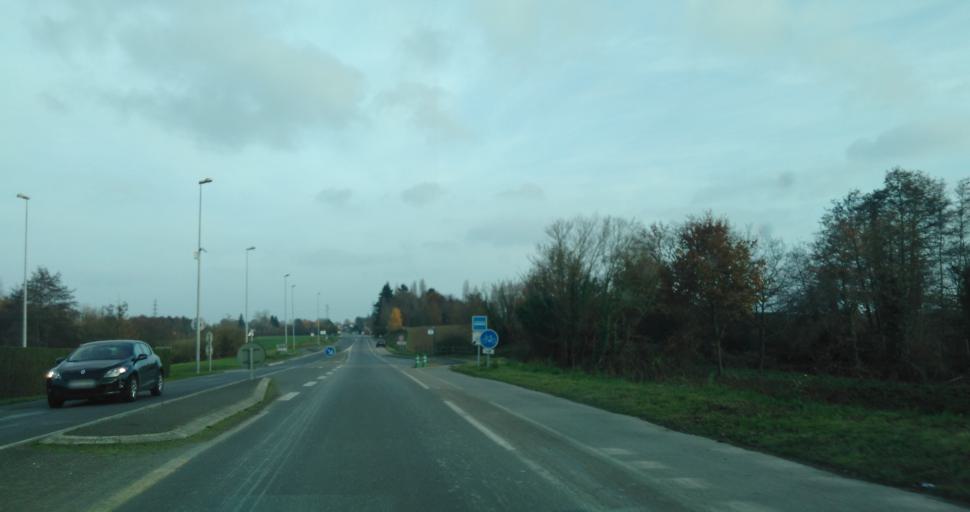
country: FR
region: Brittany
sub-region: Departement d'Ille-et-Vilaine
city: Vezin-le-Coquet
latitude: 48.1185
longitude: -1.7436
